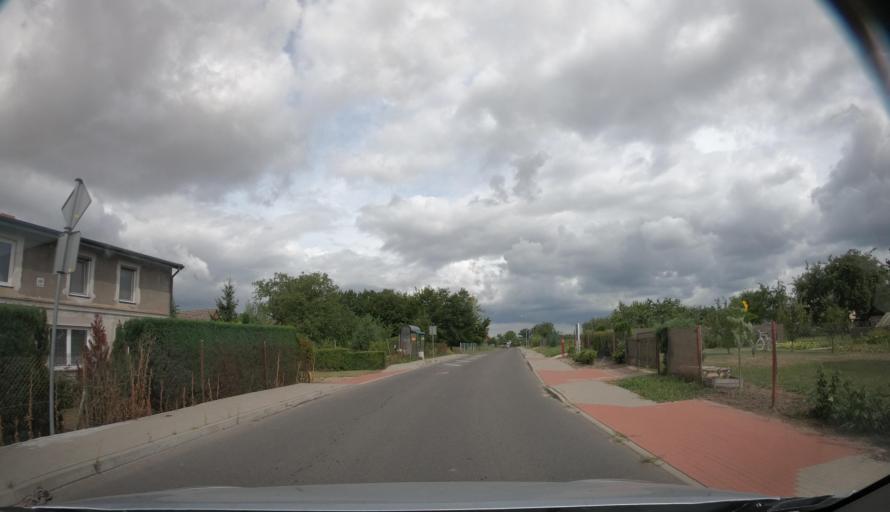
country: PL
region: West Pomeranian Voivodeship
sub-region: Koszalin
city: Koszalin
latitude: 54.1396
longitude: 16.0823
